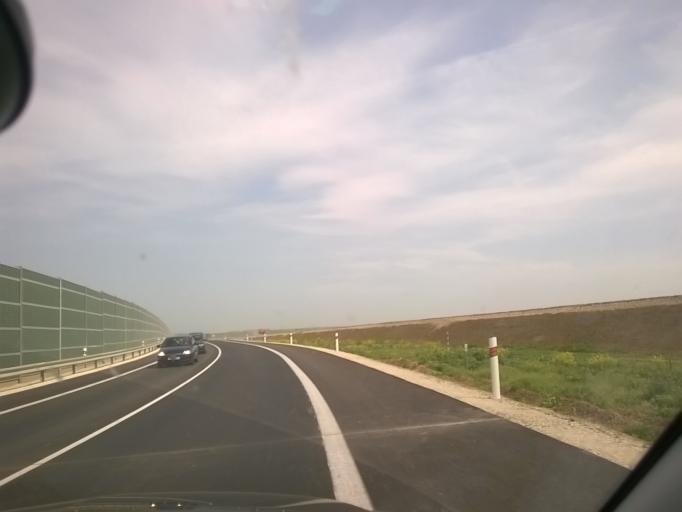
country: SK
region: Nitriansky
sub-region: Okres Nitra
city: Nitra
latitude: 48.3476
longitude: 18.0343
